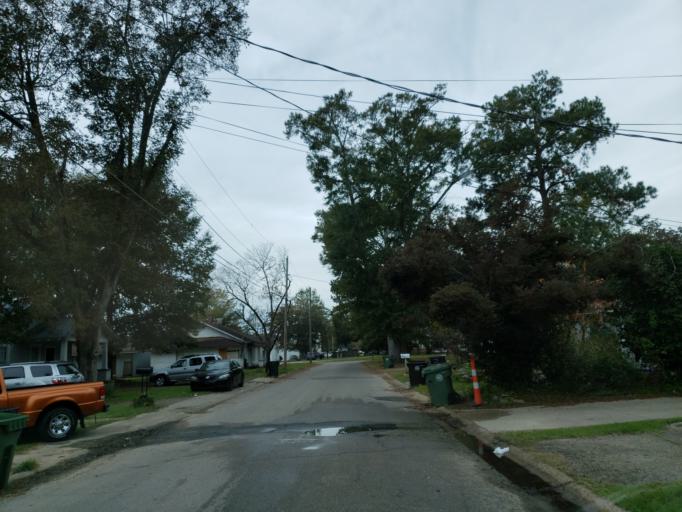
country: US
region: Mississippi
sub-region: Forrest County
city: Hattiesburg
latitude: 31.3257
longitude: -89.3030
